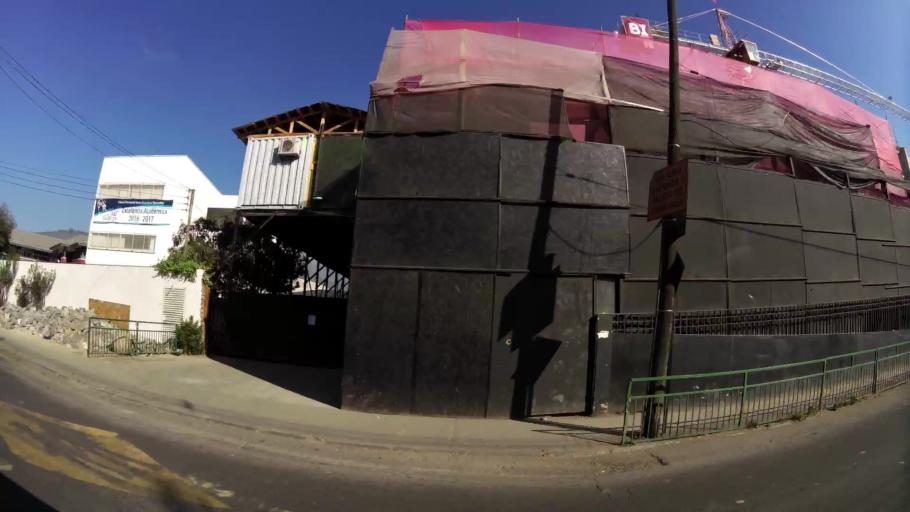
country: CL
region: Santiago Metropolitan
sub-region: Provincia de Santiago
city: Villa Presidente Frei, Nunoa, Santiago, Chile
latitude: -33.3615
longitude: -70.5045
